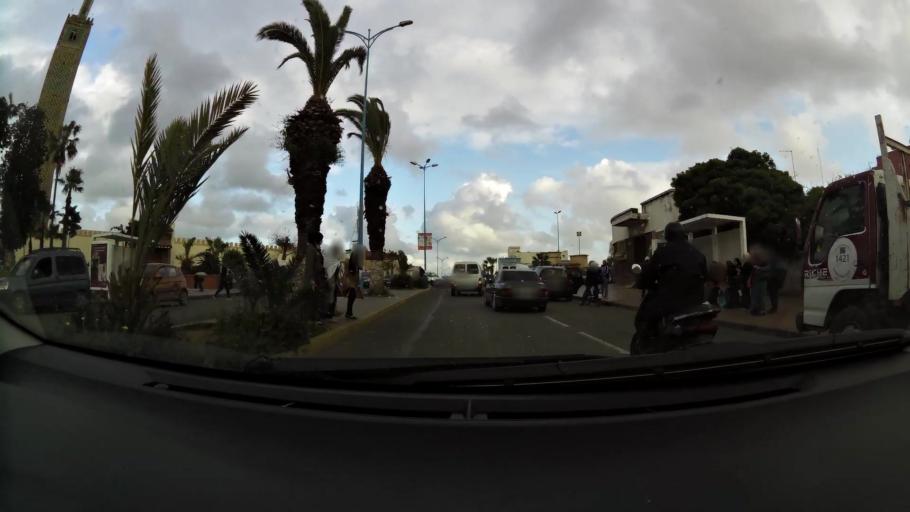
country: MA
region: Grand Casablanca
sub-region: Mohammedia
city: Mohammedia
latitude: 33.6870
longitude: -7.3904
